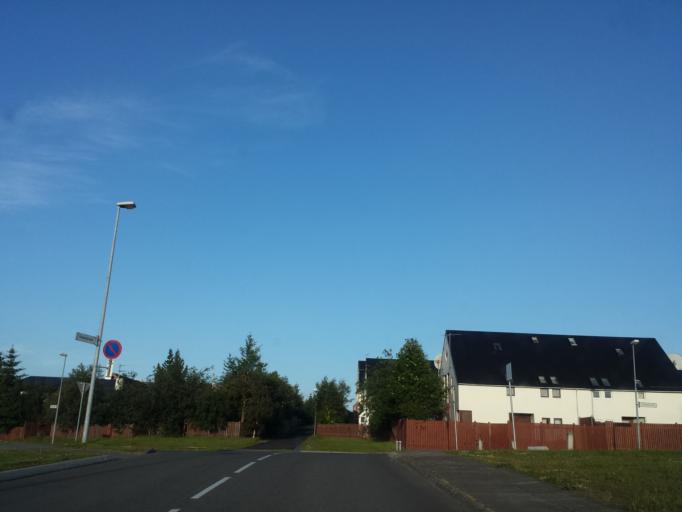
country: IS
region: Capital Region
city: Mosfellsbaer
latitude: 64.1049
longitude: -21.7832
